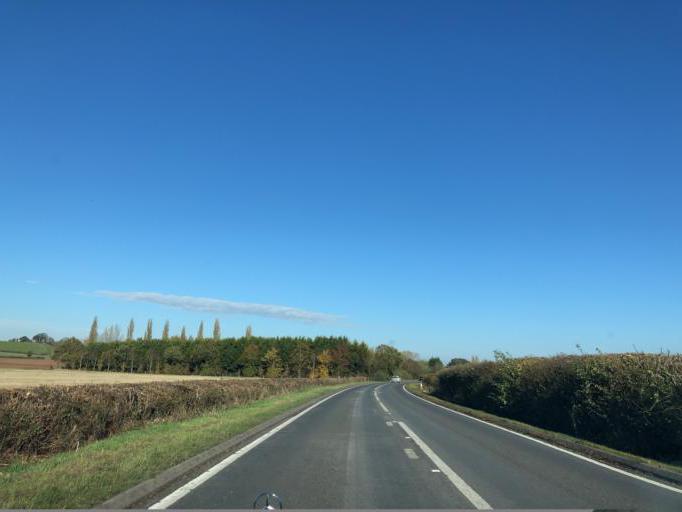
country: GB
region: England
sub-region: Warwickshire
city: Harbury
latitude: 52.2514
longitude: -1.4876
